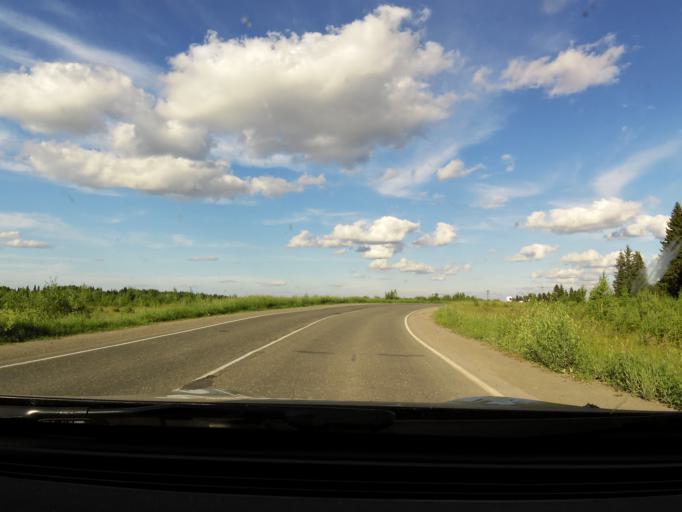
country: RU
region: Kirov
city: Omutninsk
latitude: 58.6891
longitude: 52.1651
